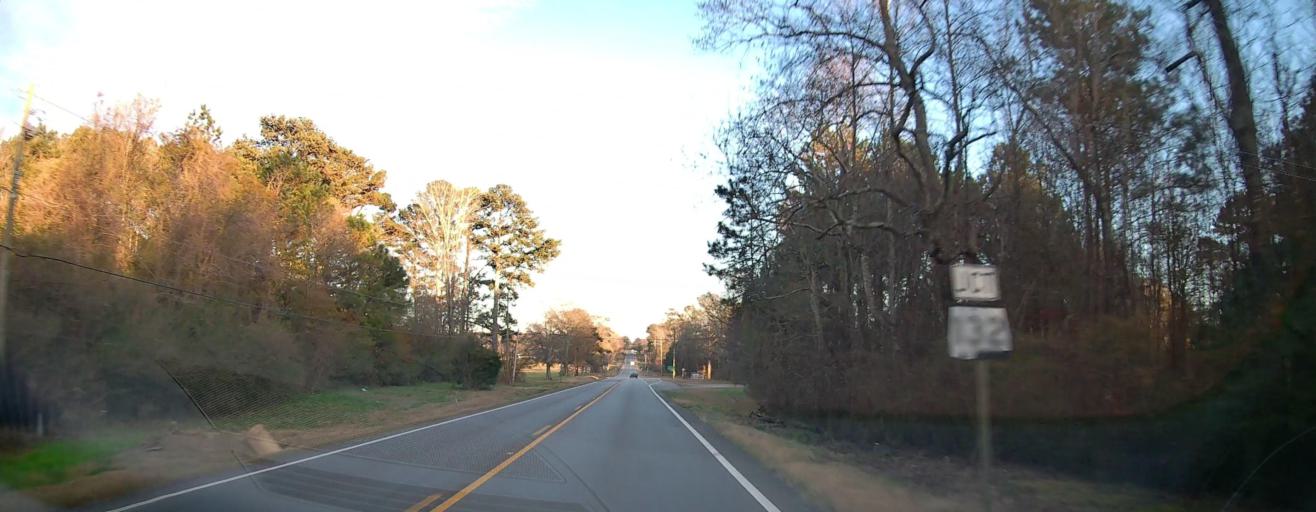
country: US
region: Alabama
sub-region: Saint Clair County
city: Steele
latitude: 34.0583
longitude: -86.2235
